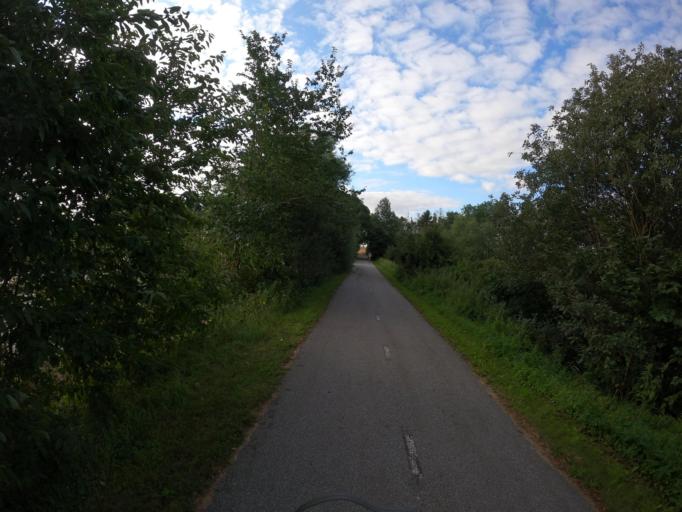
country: SE
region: Skane
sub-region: Lunds Kommun
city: Lund
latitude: 55.6794
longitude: 13.1929
